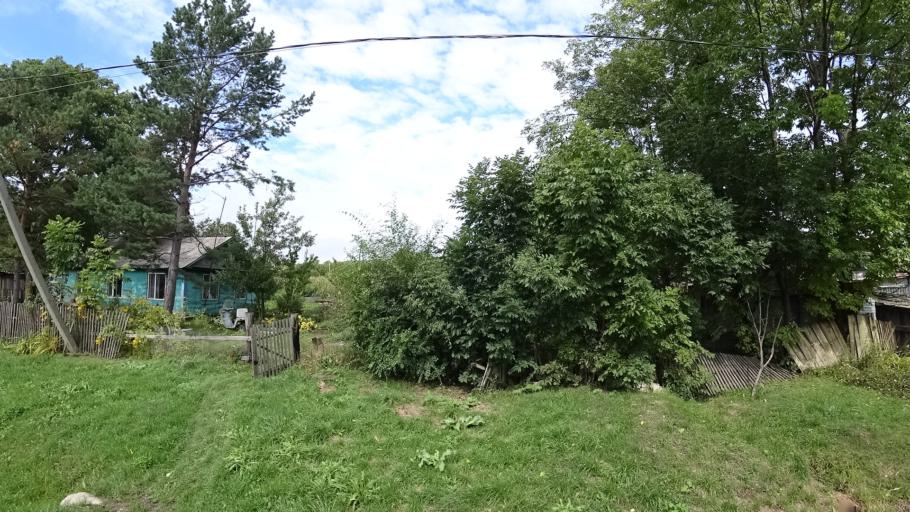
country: RU
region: Primorskiy
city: Lyalichi
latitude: 44.1390
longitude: 132.3824
